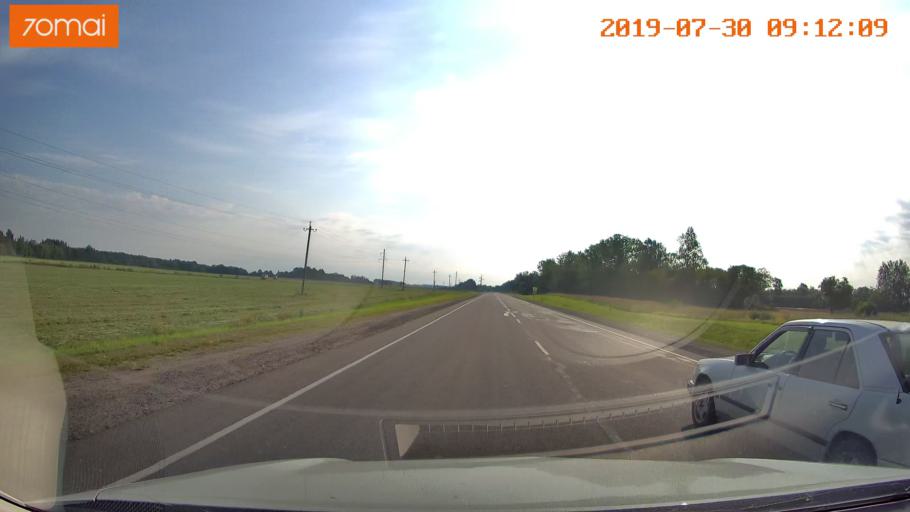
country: RU
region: Kaliningrad
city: Nesterov
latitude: 54.6156
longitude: 22.4670
